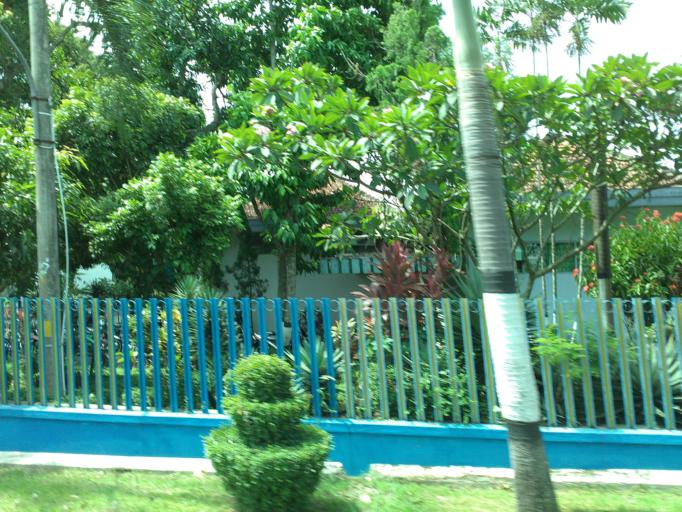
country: ID
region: Central Java
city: Klaten
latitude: -7.7036
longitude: 110.5935
